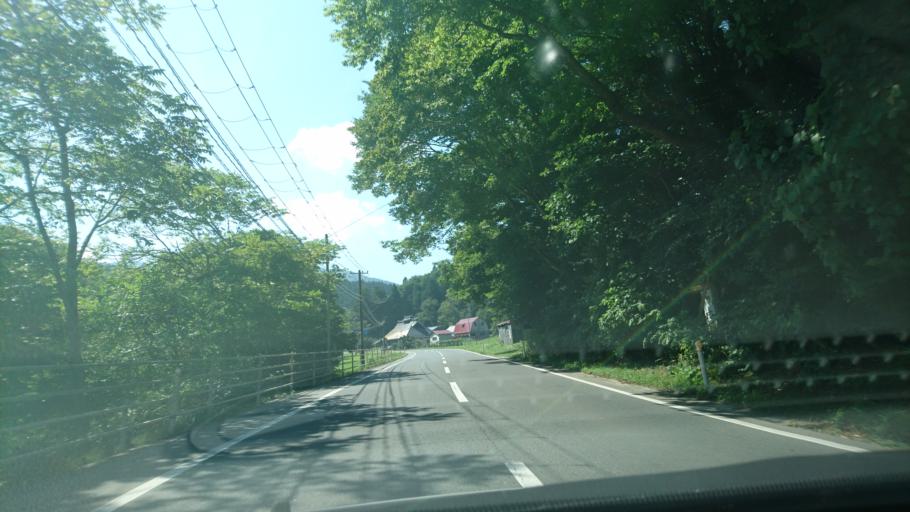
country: JP
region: Iwate
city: Ofunato
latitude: 39.0203
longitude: 141.5512
